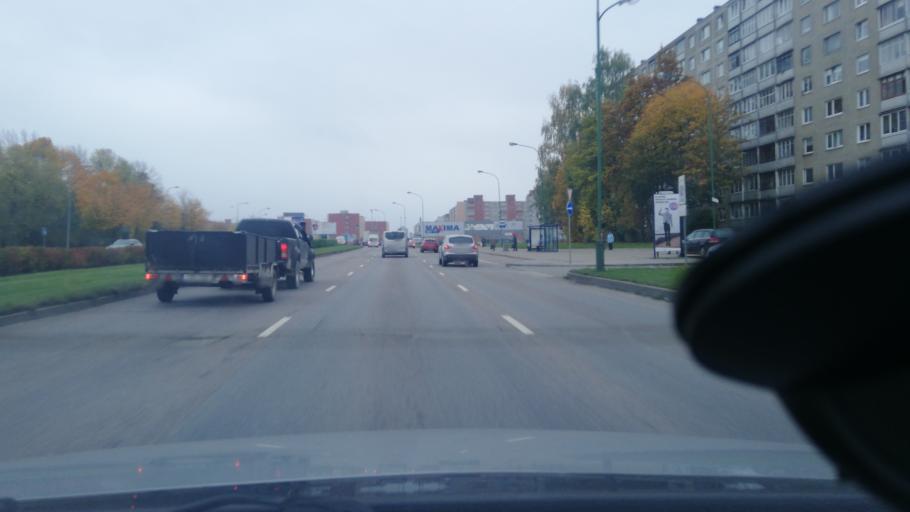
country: LT
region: Klaipedos apskritis
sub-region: Klaipeda
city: Klaipeda
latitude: 55.6795
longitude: 21.1874
